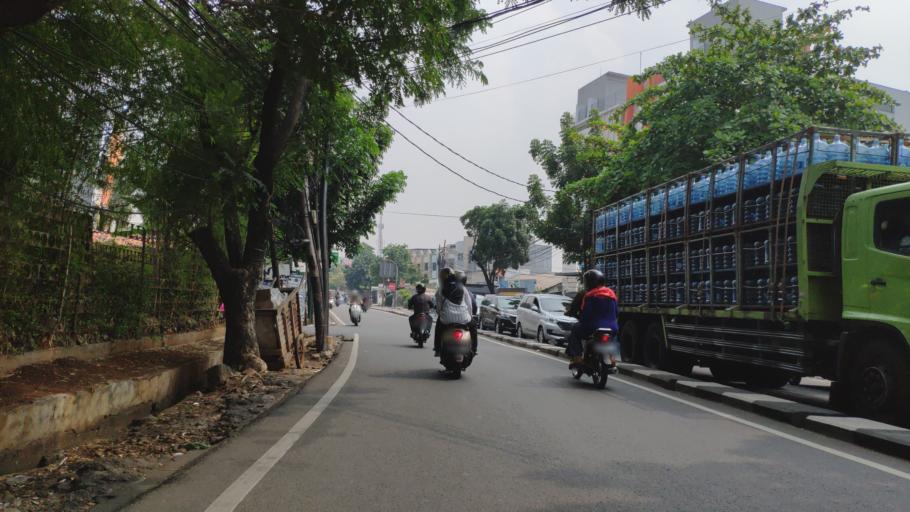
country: ID
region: Banten
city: South Tangerang
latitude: -6.2732
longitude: 106.7747
